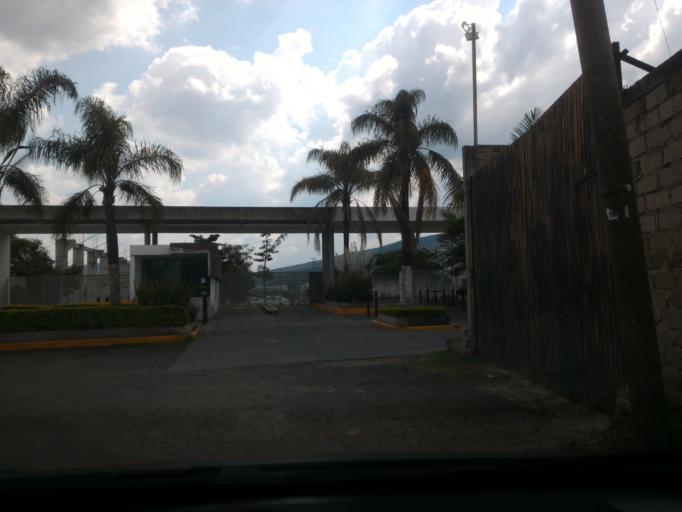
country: MX
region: Jalisco
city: Nuevo Mexico
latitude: 20.6987
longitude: -103.4707
